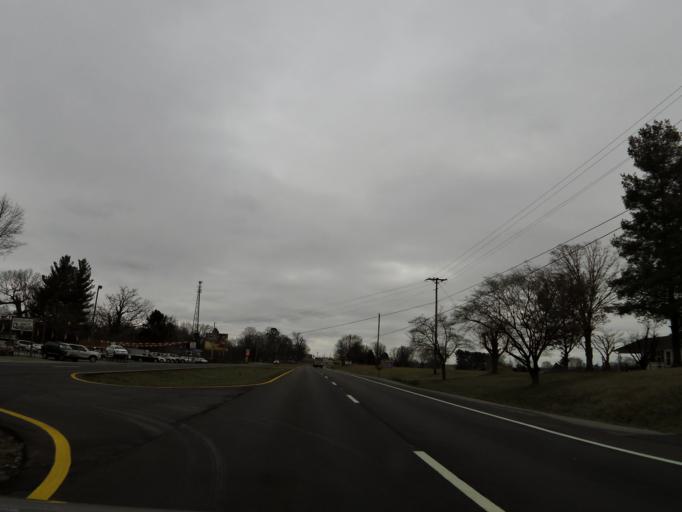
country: US
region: Tennessee
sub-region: Jefferson County
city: Jefferson City
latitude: 36.1523
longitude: -83.4304
